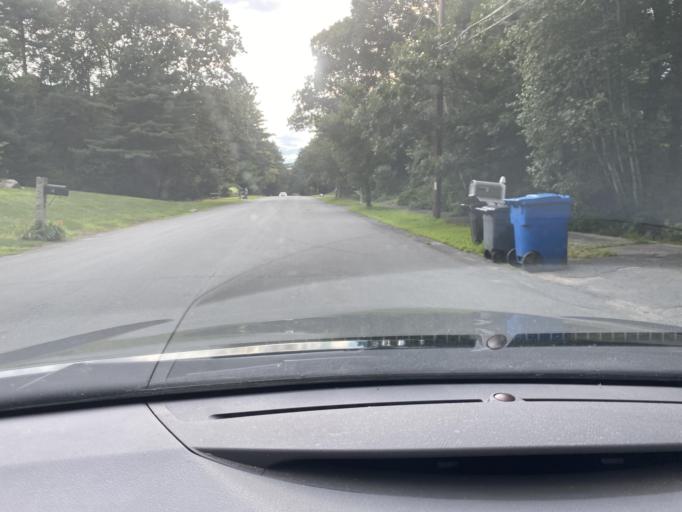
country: US
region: Massachusetts
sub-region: Norfolk County
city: Walpole
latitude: 42.1782
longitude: -71.2544
